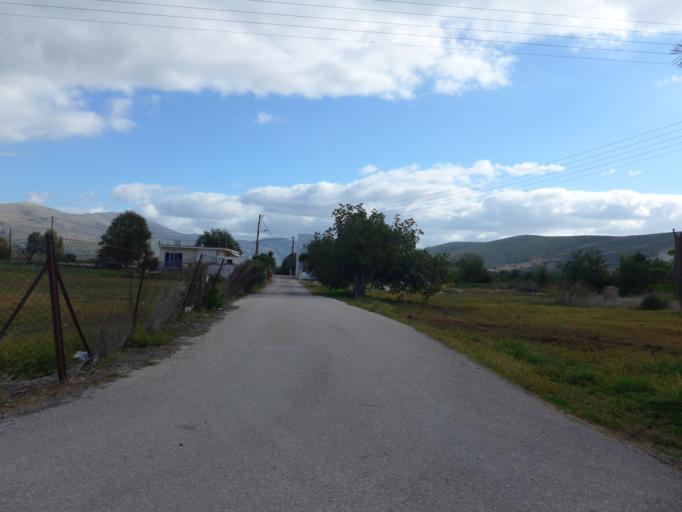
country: GR
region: Peloponnese
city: Asklipieio
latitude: 37.4827
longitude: 22.9940
